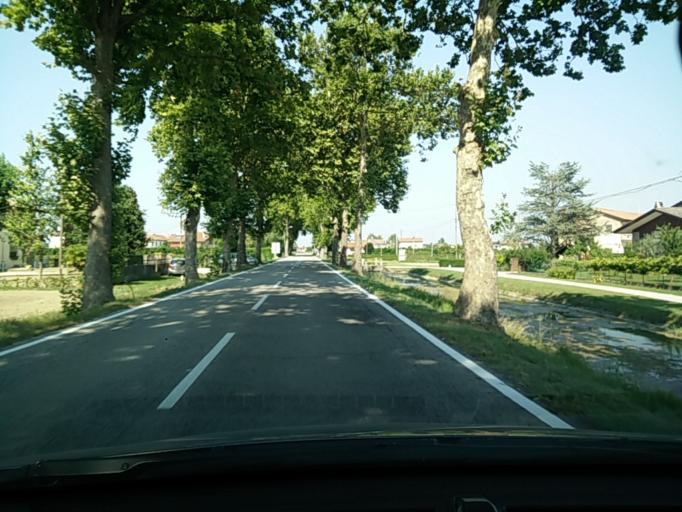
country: IT
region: Veneto
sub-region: Provincia di Venezia
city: Crepaldo
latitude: 45.6108
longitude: 12.7124
